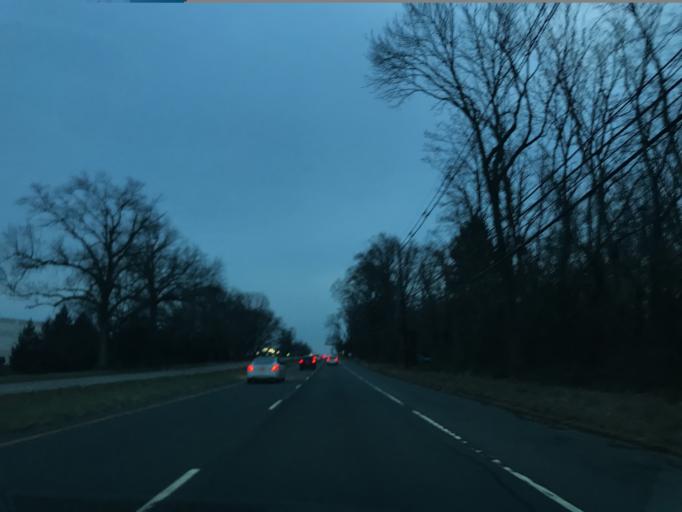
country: US
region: New Jersey
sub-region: Middlesex County
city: Cranbury
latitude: 40.3249
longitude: -74.5072
